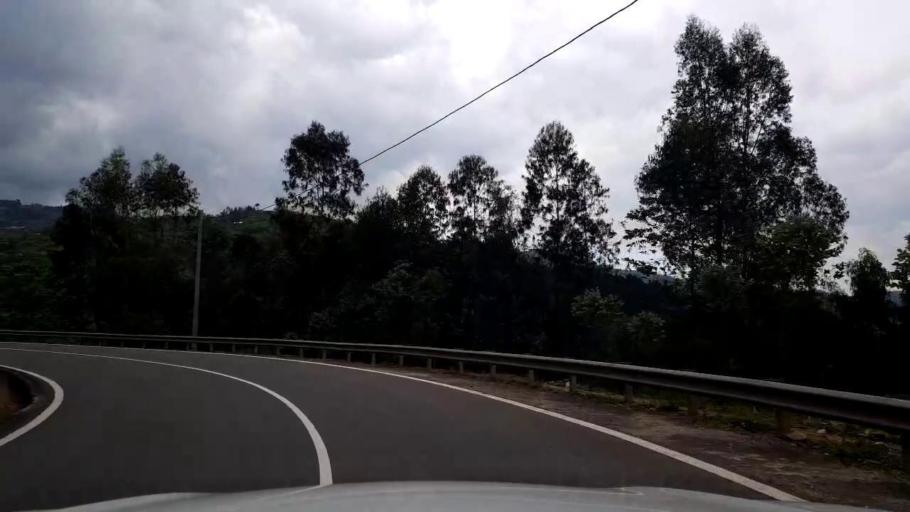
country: RW
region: Western Province
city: Kibuye
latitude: -1.9264
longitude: 29.3691
